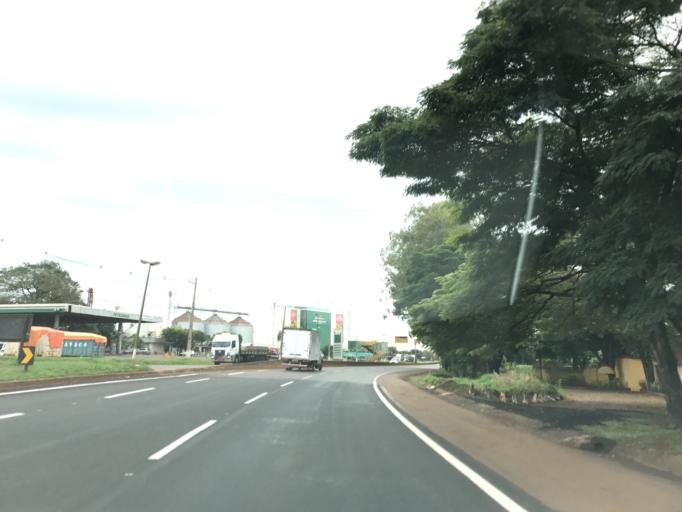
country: BR
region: Parana
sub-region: Rolandia
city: Rolandia
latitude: -23.3576
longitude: -51.3954
